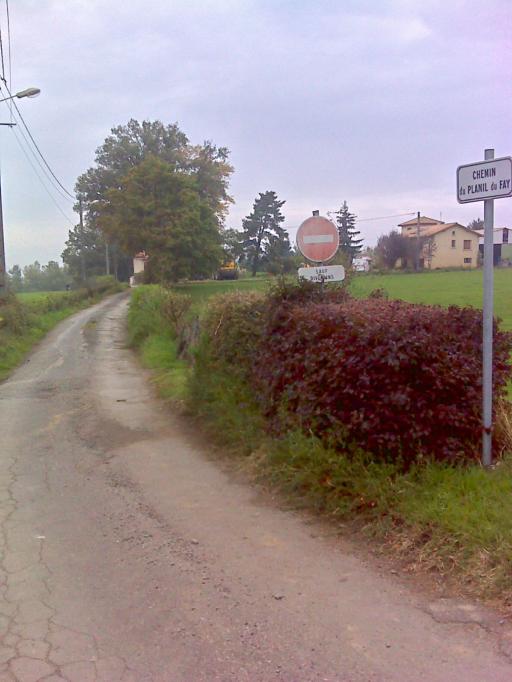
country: FR
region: Rhone-Alpes
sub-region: Departement de la Loire
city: La Talaudiere
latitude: 45.4705
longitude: 4.4458
